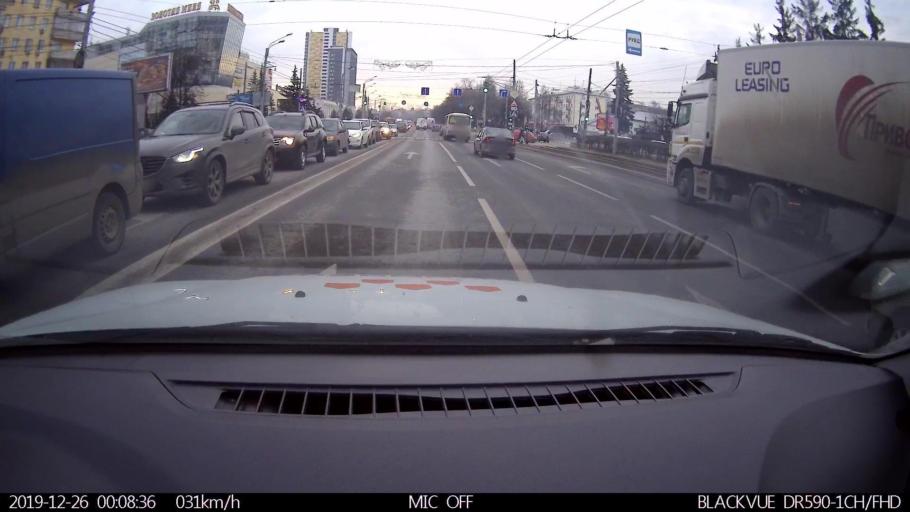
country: RU
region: Nizjnij Novgorod
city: Neklyudovo
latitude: 56.3484
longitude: 43.8688
